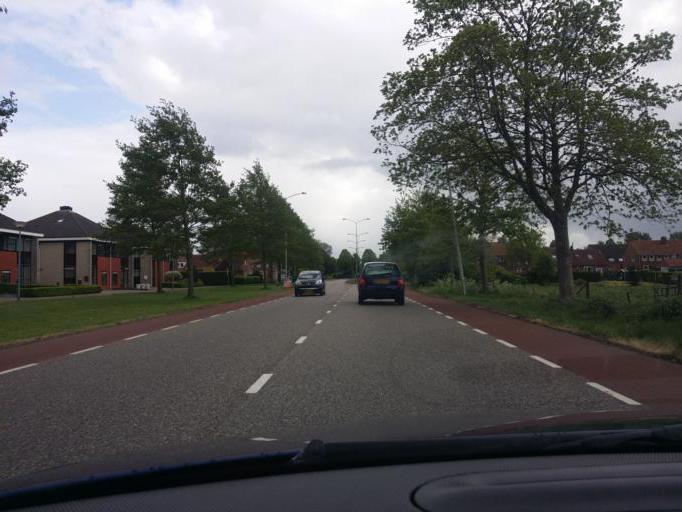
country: NL
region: Groningen
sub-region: Gemeente Hoogezand-Sappemeer
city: Hoogezand
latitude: 53.1585
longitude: 6.7399
